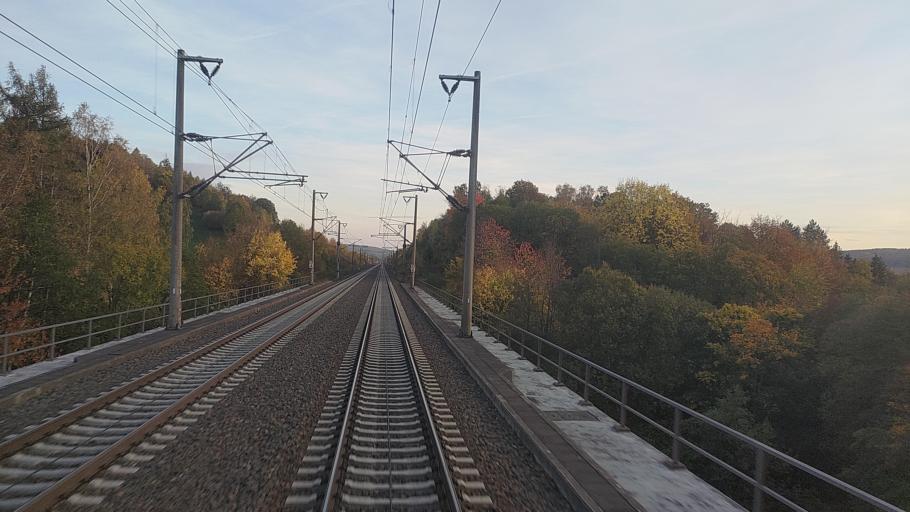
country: DE
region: Lower Saxony
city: Sibbesse
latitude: 52.0700
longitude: 9.9032
